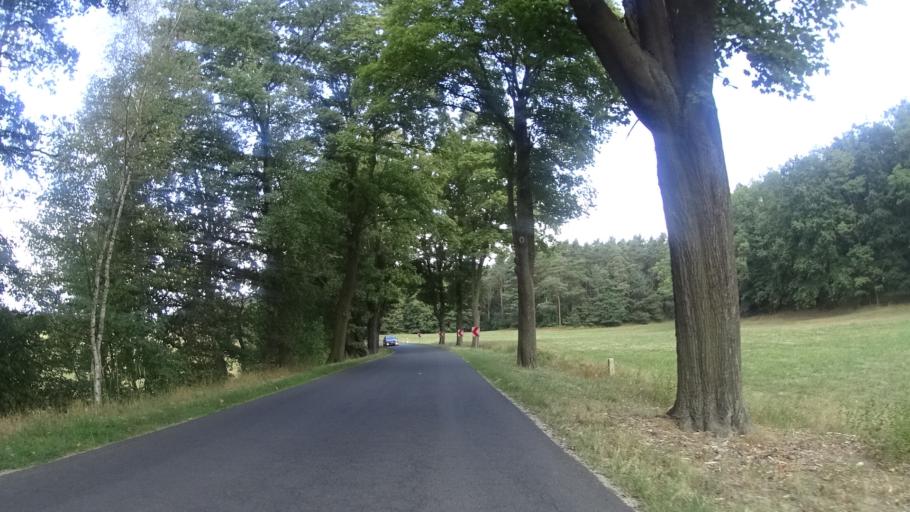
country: PL
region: Lubusz
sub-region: Powiat zarski
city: Przewoz
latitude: 51.4834
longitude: 14.9272
